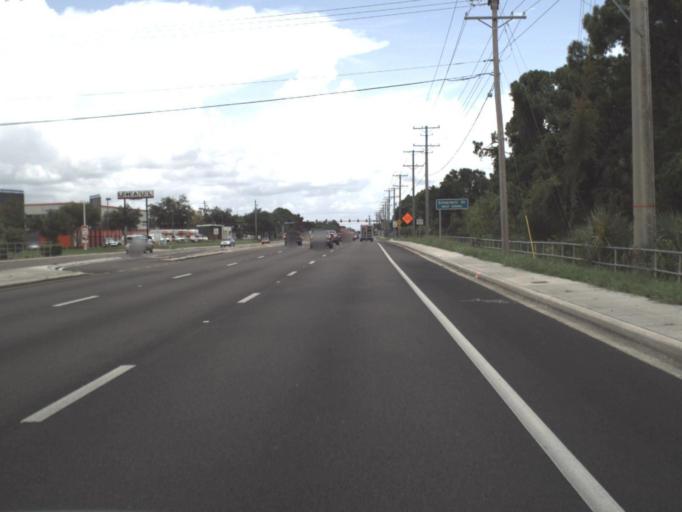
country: US
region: Florida
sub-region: Hillsborough County
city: Town 'n' Country
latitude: 28.0138
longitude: -82.6137
